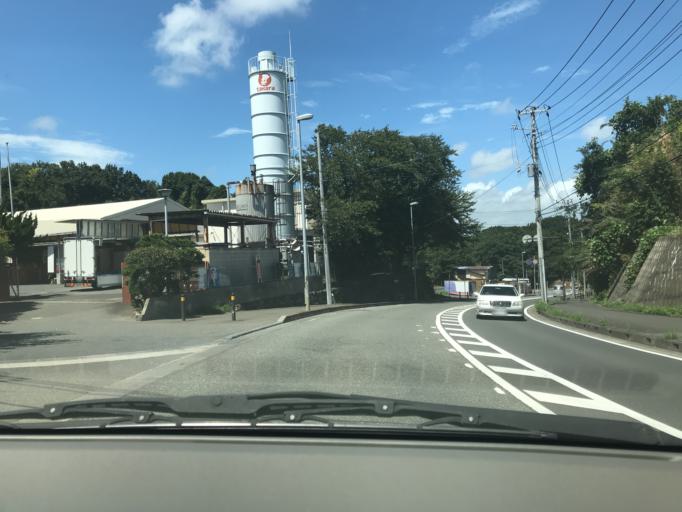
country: JP
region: Kanagawa
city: Fujisawa
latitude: 35.3676
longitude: 139.4590
